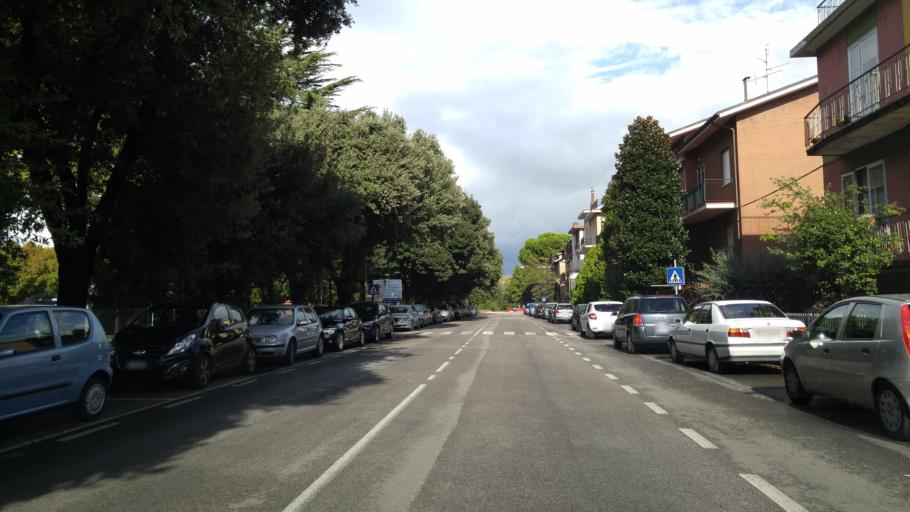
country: IT
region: The Marches
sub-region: Provincia di Pesaro e Urbino
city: Pesaro
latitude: 43.9028
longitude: 12.8951
